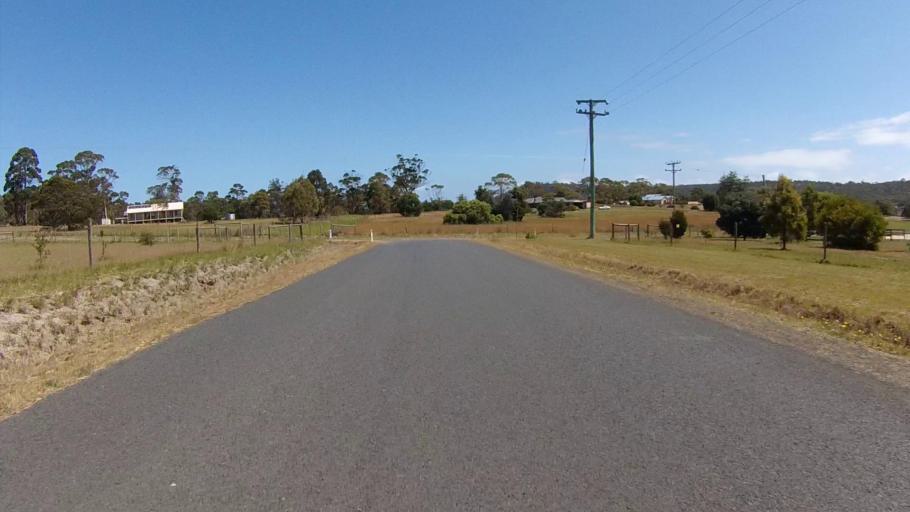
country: AU
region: Tasmania
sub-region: Clarence
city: Sandford
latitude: -42.9564
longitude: 147.4827
